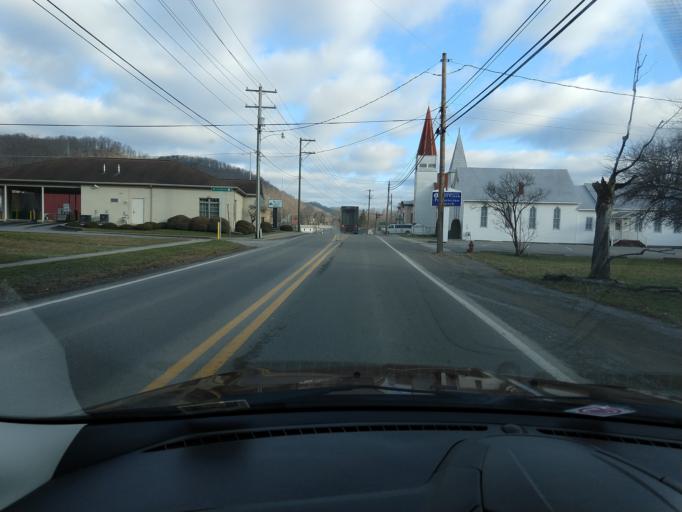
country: US
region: West Virginia
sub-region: Randolph County
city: Elkins
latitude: 38.7305
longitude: -79.9706
